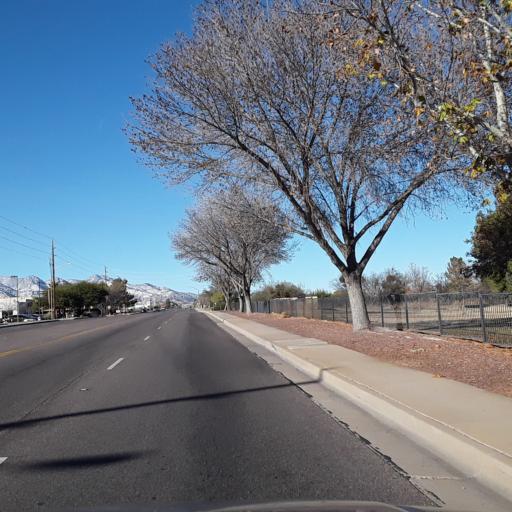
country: US
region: Arizona
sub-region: Cochise County
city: Sierra Vista
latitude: 31.5547
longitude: -110.2687
